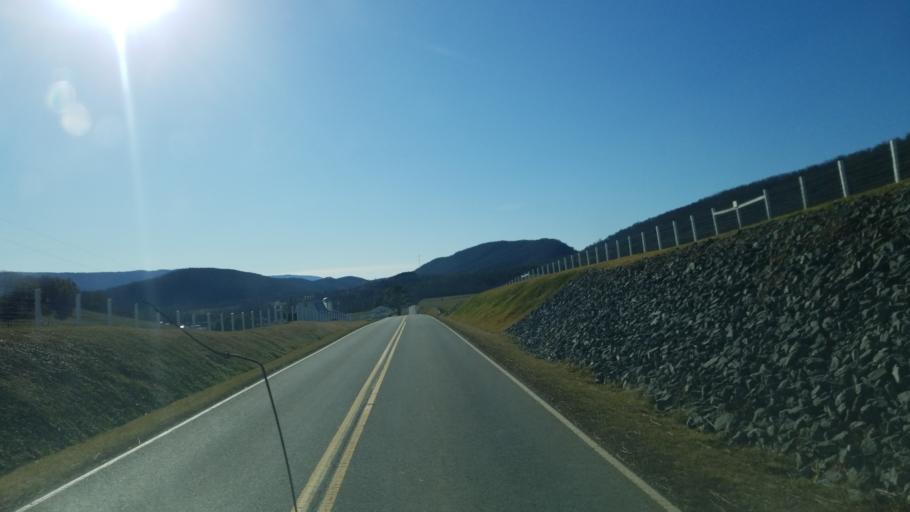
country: US
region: Virginia
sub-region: Pulaski County
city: Pulaski
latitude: 37.1770
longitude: -80.8768
